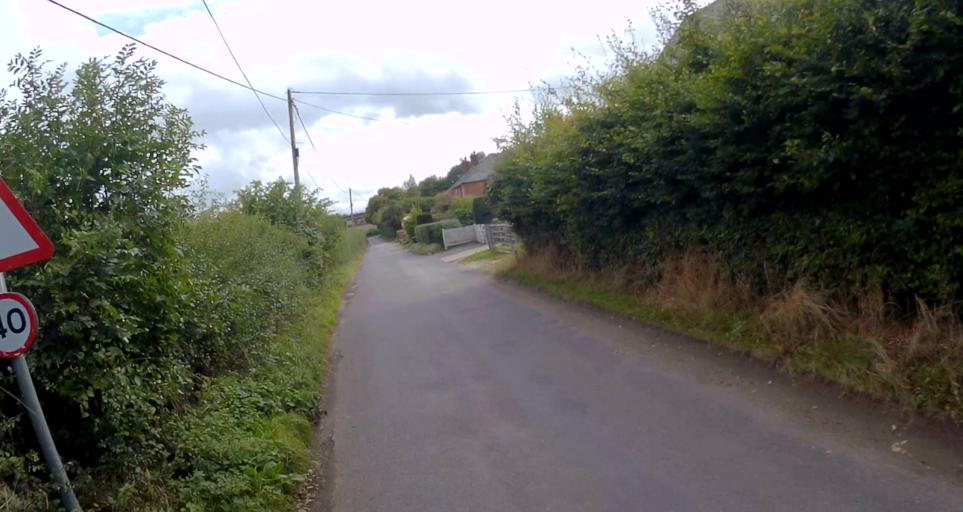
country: GB
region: England
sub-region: Hampshire
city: Kings Worthy
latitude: 51.0835
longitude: -1.1833
